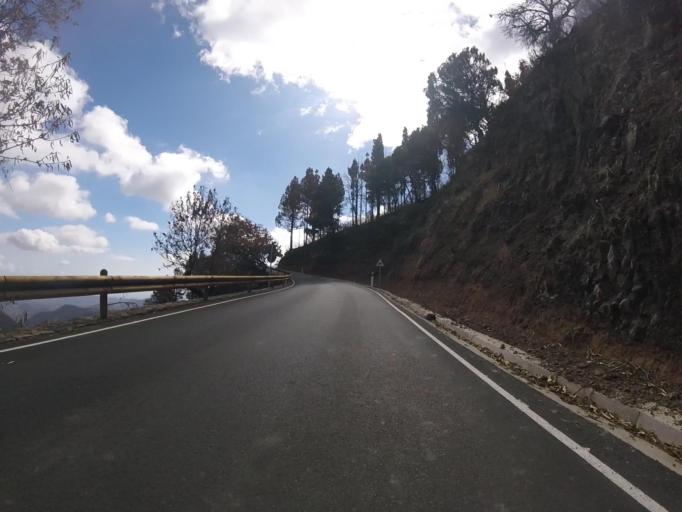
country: ES
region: Canary Islands
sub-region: Provincia de Las Palmas
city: Tejeda
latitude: 28.0029
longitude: -15.5948
